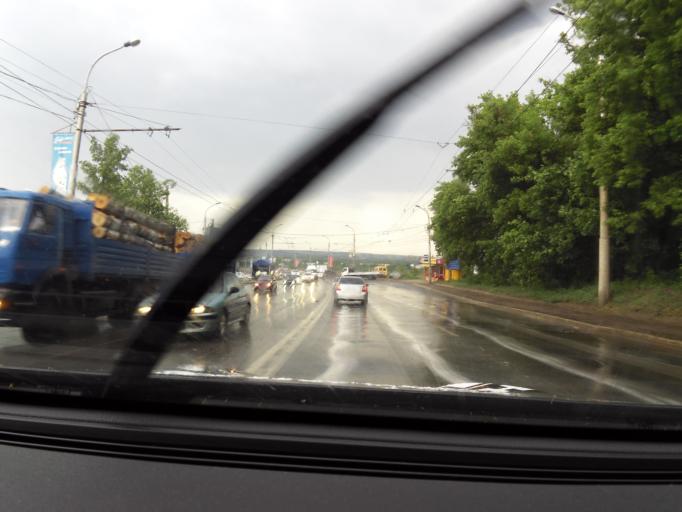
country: RU
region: Bashkortostan
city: Ufa
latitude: 54.7541
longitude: 55.9702
